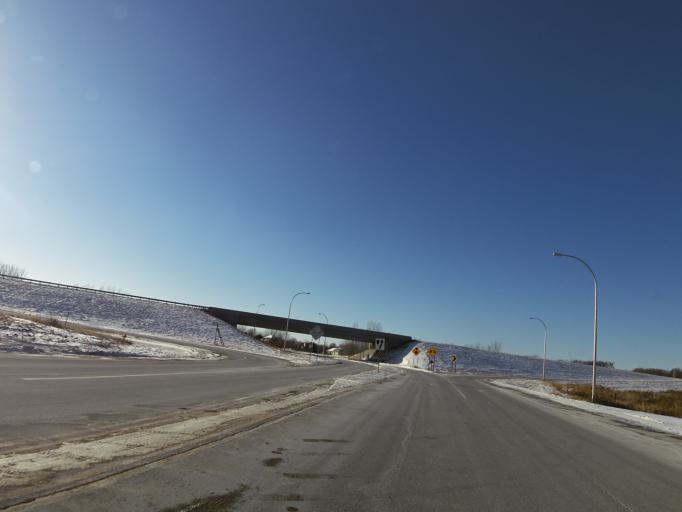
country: US
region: Minnesota
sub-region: Scott County
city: Shakopee
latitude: 44.7466
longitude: -93.4992
